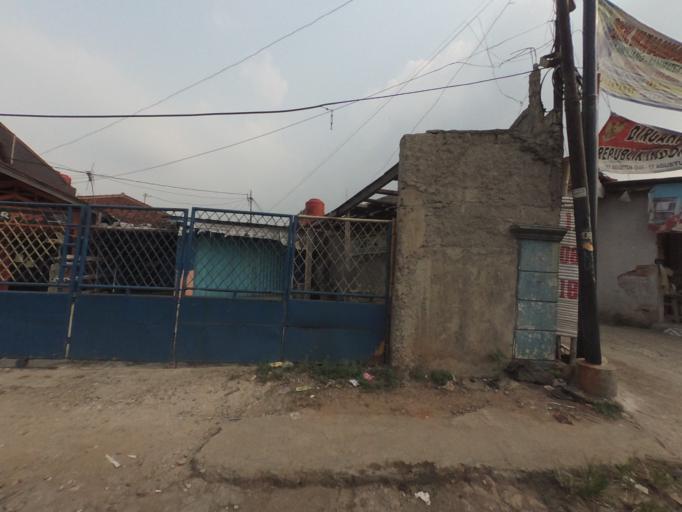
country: ID
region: West Java
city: Ciampea
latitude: -6.5656
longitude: 106.6745
